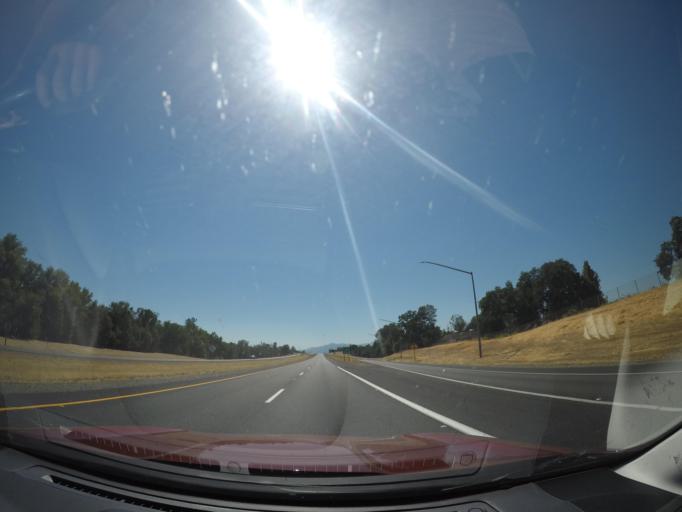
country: US
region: California
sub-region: Shasta County
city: Shasta Lake
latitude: 40.6219
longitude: -122.3144
